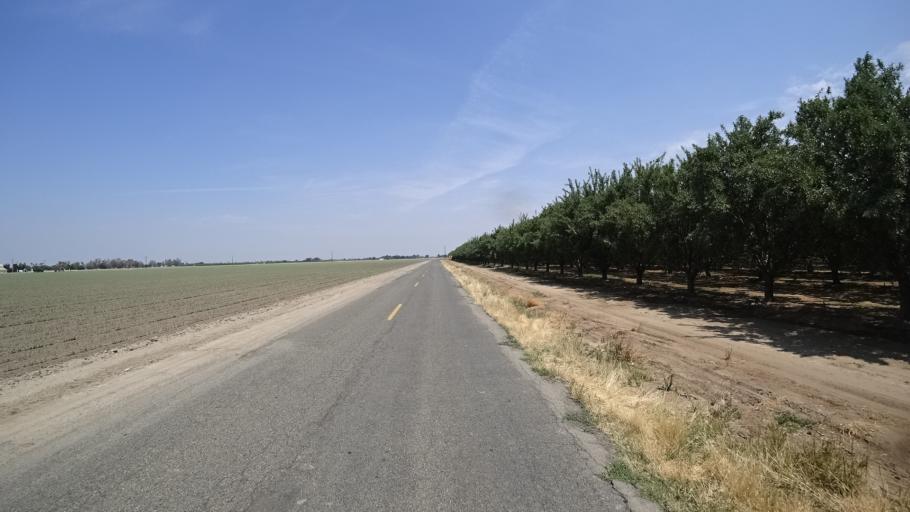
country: US
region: California
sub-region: Kings County
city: Lemoore
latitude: 36.3252
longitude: -119.7943
